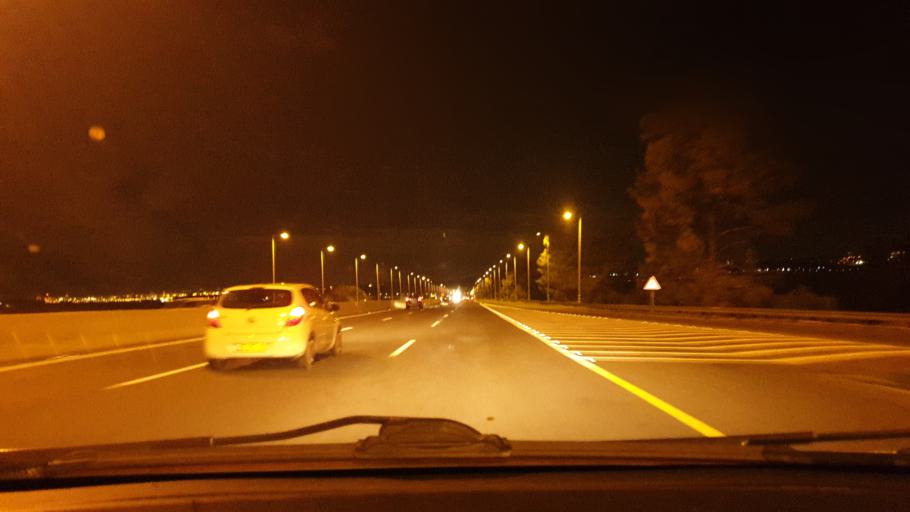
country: IL
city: Nof Ayalon
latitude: 31.8410
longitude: 34.9864
